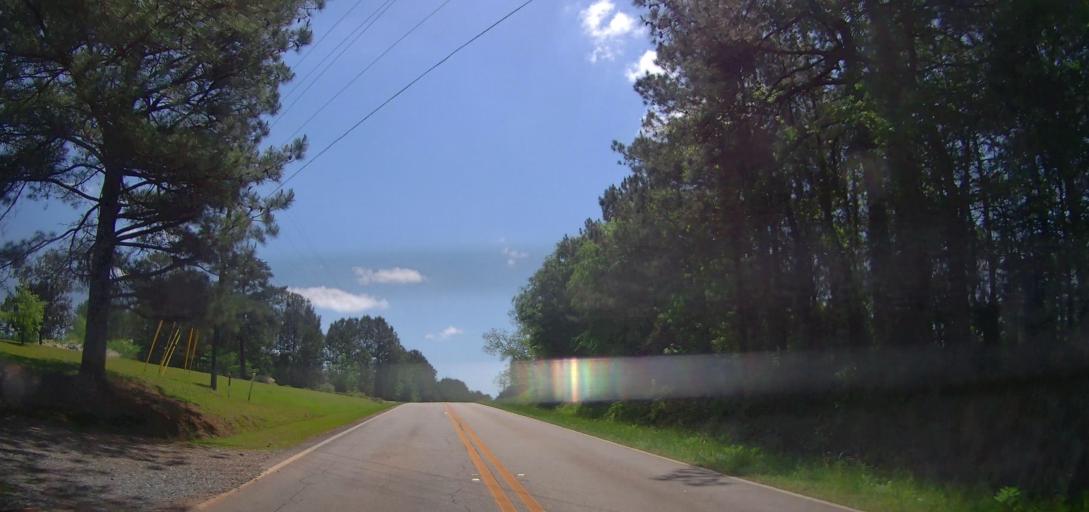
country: US
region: Georgia
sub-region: Jones County
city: Gray
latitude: 33.0543
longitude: -83.5979
